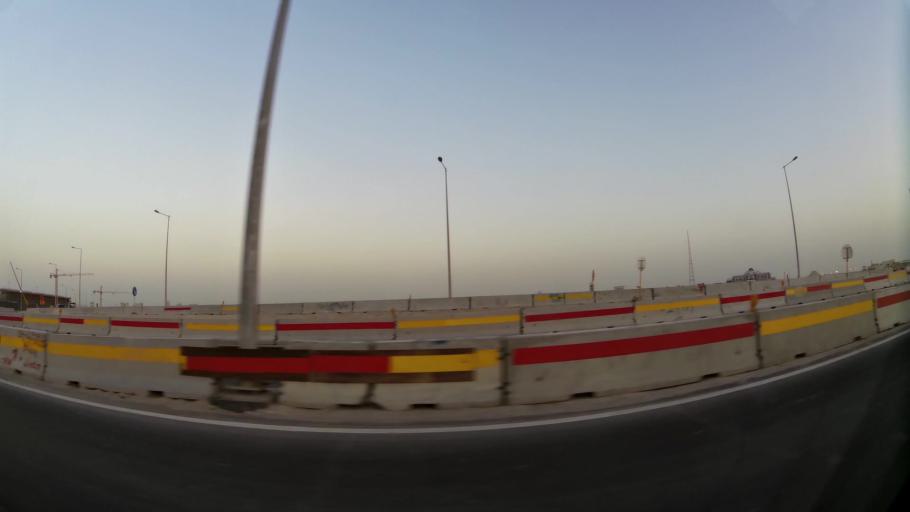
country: QA
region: Baladiyat ar Rayyan
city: Ar Rayyan
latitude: 25.2942
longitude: 51.4684
